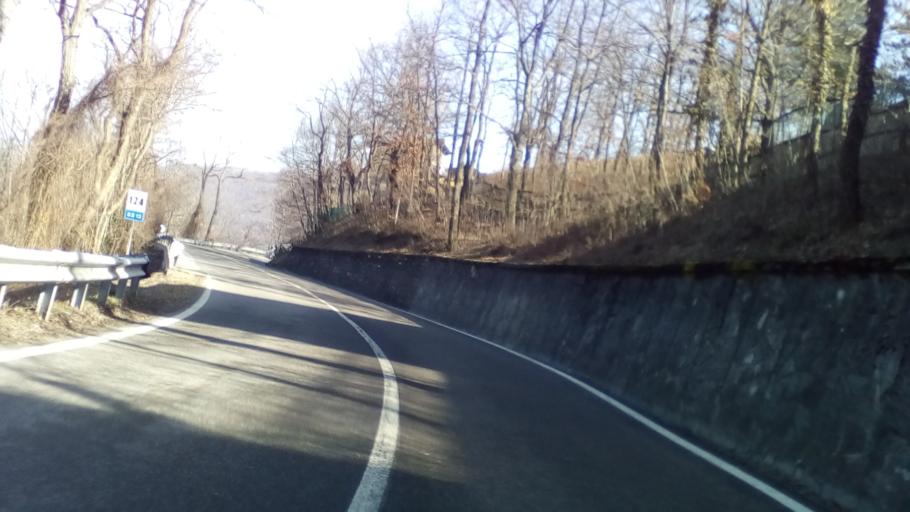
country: IT
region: Emilia-Romagna
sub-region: Provincia di Modena
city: Lama
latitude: 44.3057
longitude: 10.7233
